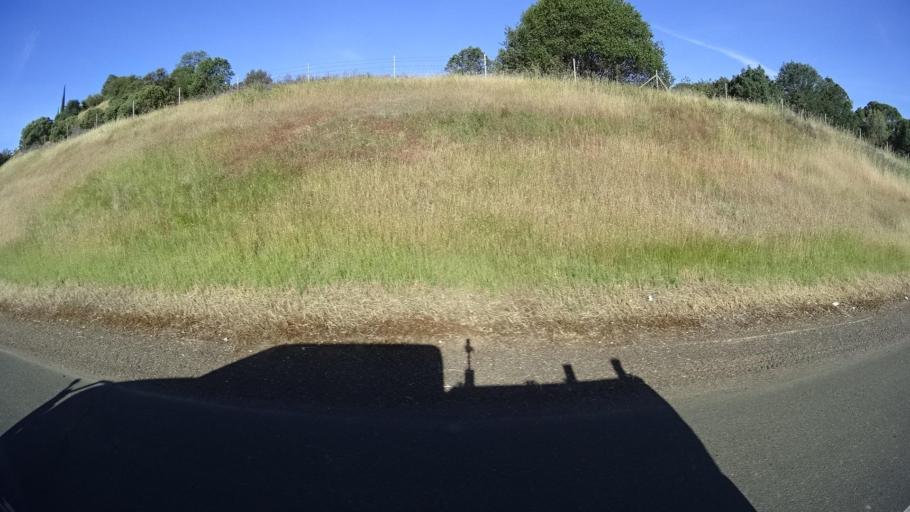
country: US
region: California
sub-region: Lake County
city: Lakeport
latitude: 39.0486
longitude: -122.9318
